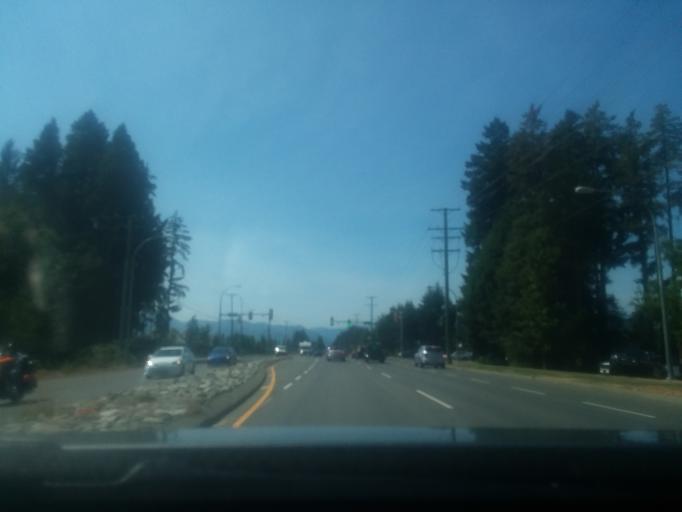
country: CA
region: British Columbia
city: Courtenay
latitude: 49.7133
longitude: -124.9602
